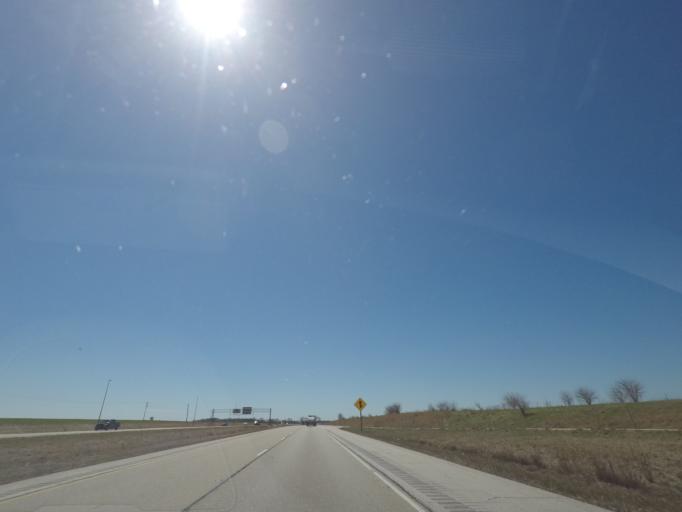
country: US
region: Illinois
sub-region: McLean County
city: Twin Grove
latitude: 40.4059
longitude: -89.0559
